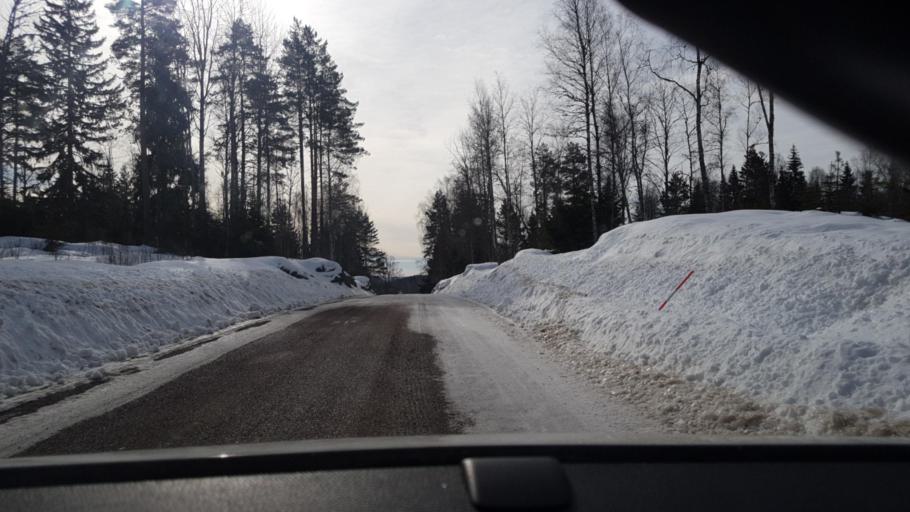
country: NO
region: Ostfold
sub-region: Romskog
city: Romskog
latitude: 59.7401
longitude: 12.0573
